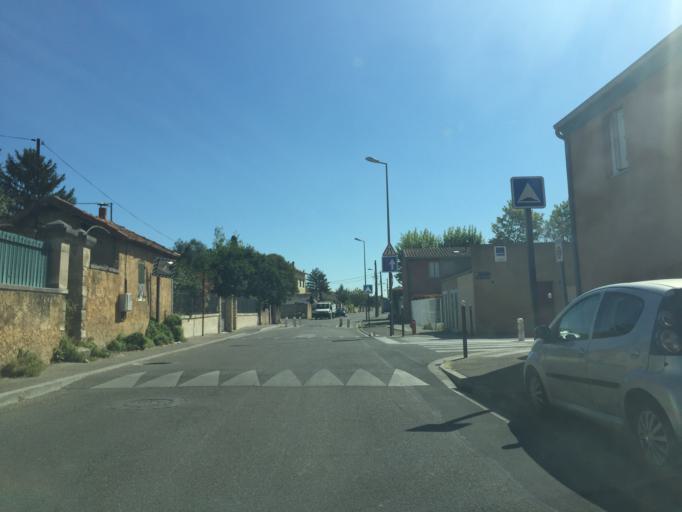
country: FR
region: Provence-Alpes-Cote d'Azur
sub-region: Departement du Vaucluse
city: Avignon
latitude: 43.9553
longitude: 4.8264
